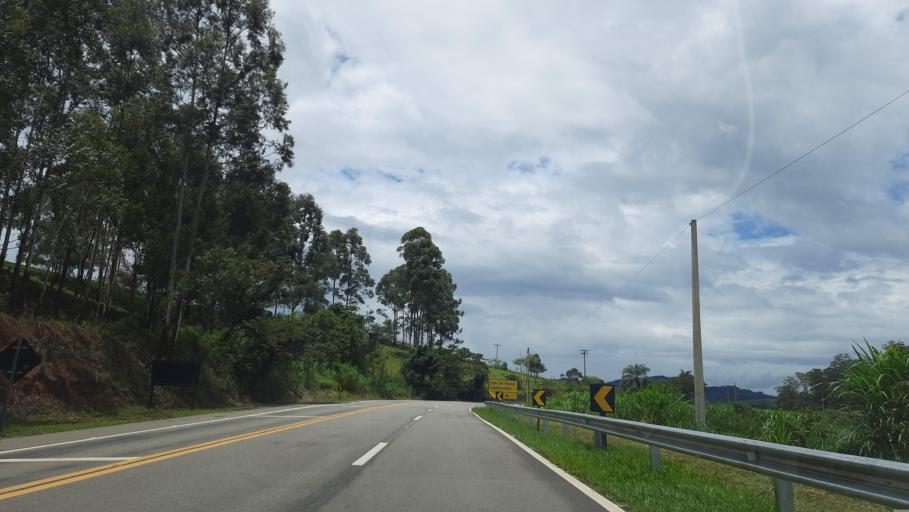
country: BR
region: Sao Paulo
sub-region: Vargem Grande Do Sul
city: Vargem Grande do Sul
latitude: -21.7996
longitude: -46.8193
